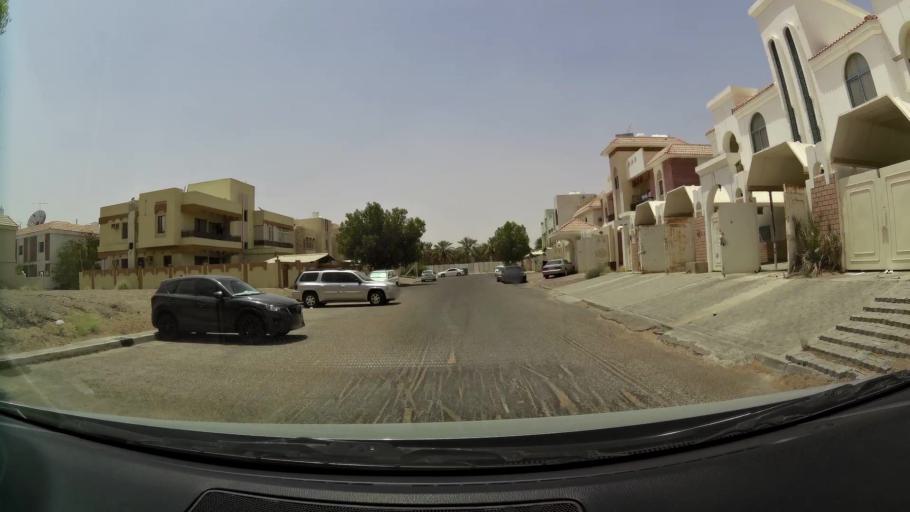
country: AE
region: Abu Dhabi
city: Al Ain
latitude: 24.2082
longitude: 55.7254
